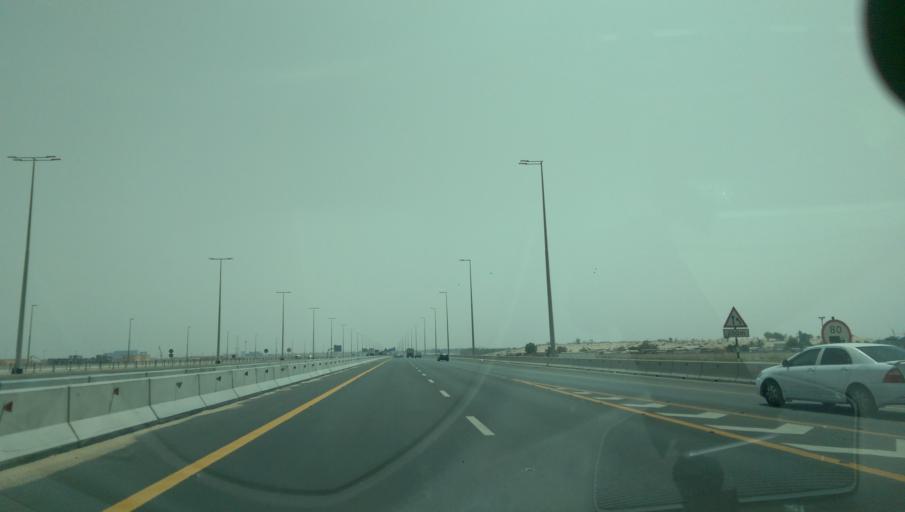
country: AE
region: Abu Dhabi
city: Abu Dhabi
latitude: 24.2968
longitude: 54.5796
